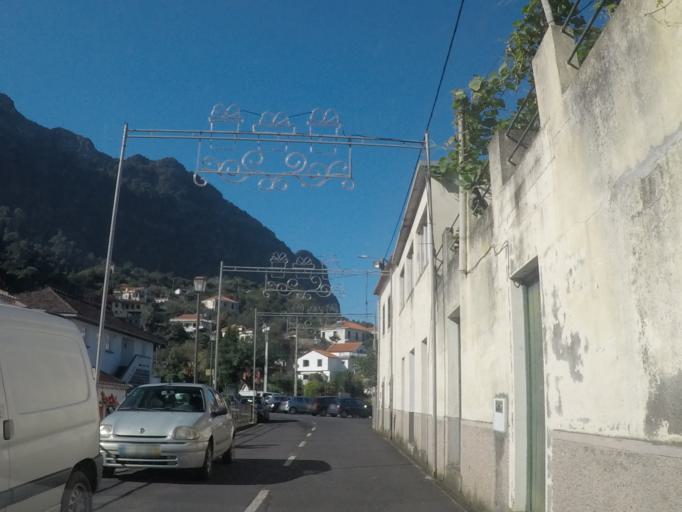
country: PT
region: Madeira
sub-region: Santana
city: Santana
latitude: 32.8267
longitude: -16.9556
